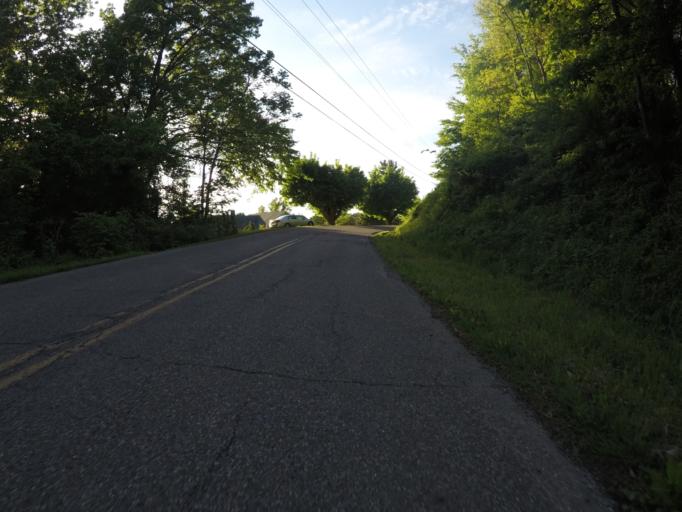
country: US
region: West Virginia
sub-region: Cabell County
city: Huntington
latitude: 38.5523
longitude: -82.4266
